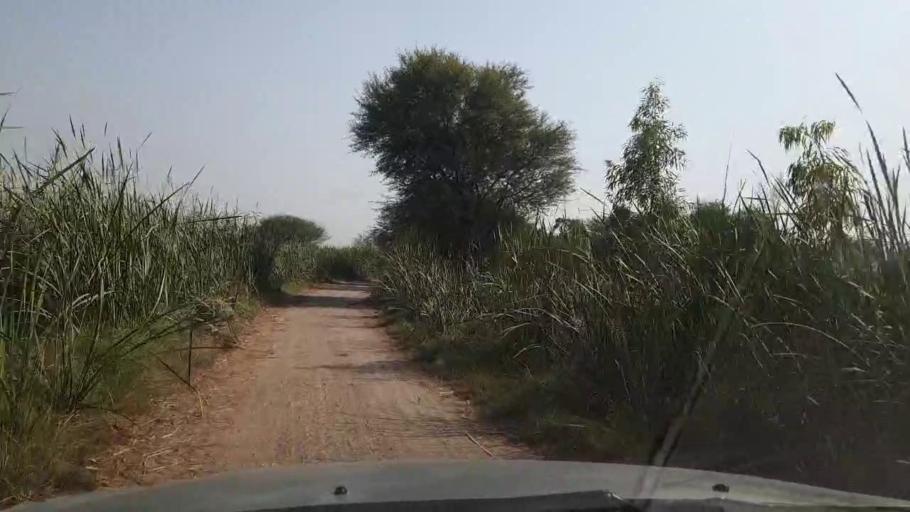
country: PK
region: Sindh
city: Bulri
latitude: 24.9031
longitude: 68.3760
